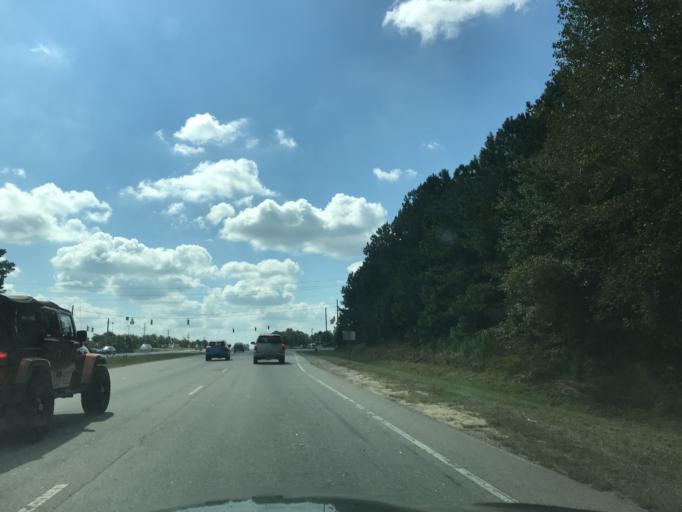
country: US
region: North Carolina
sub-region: Franklin County
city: Youngsville
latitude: 36.0428
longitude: -78.4965
